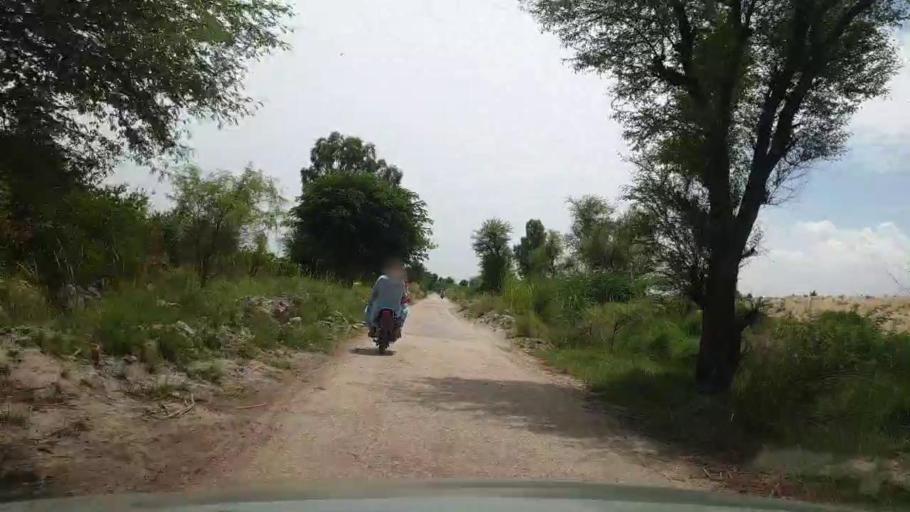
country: PK
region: Sindh
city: Bozdar
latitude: 27.0711
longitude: 68.9684
